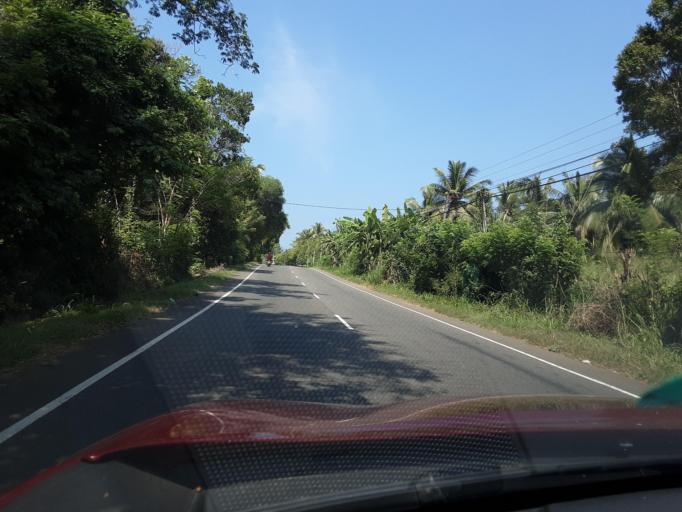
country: LK
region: Uva
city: Badulla
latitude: 7.1885
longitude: 81.0366
